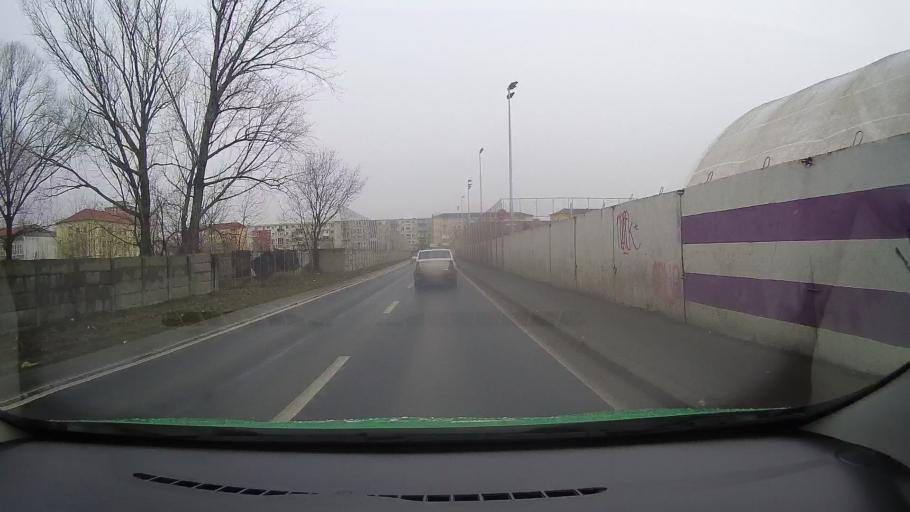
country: RO
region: Timis
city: Timisoara
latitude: 45.7417
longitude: 21.2479
